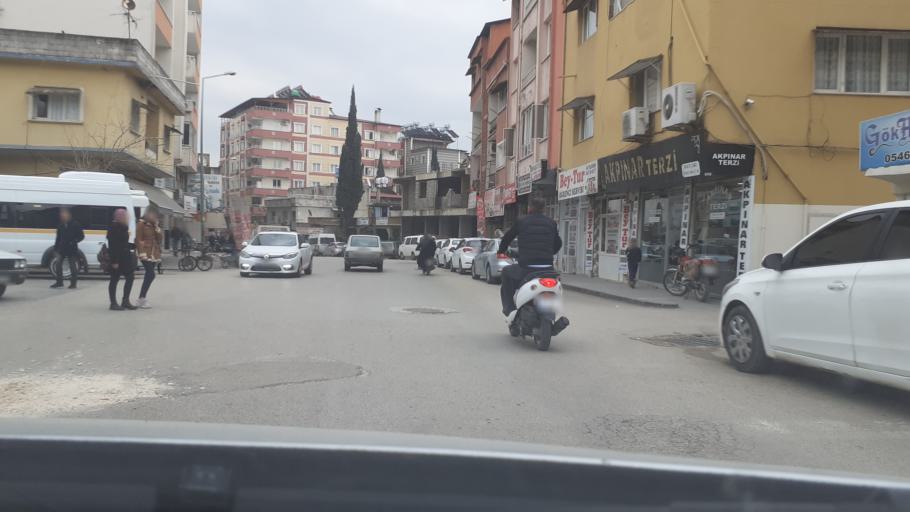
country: TR
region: Hatay
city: Kirikhan
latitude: 36.4970
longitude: 36.3576
